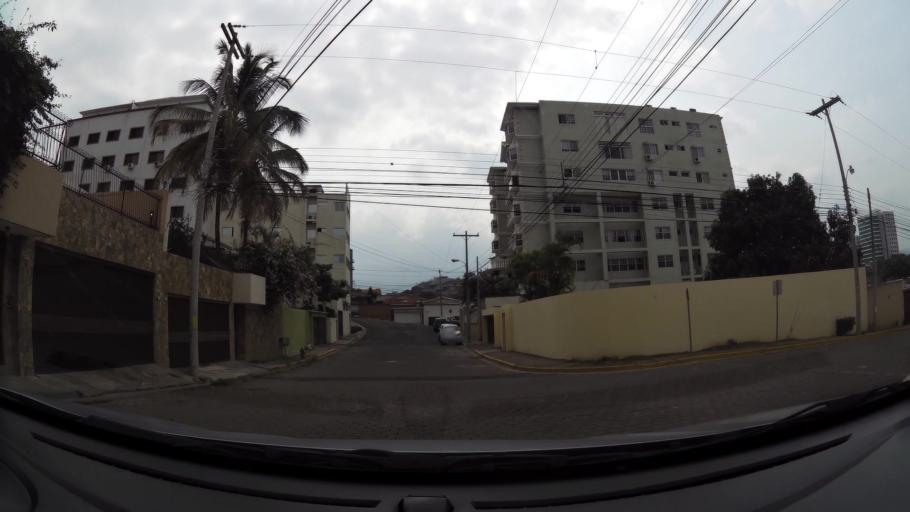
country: HN
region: Francisco Morazan
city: Tegucigalpa
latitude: 14.0916
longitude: -87.1801
